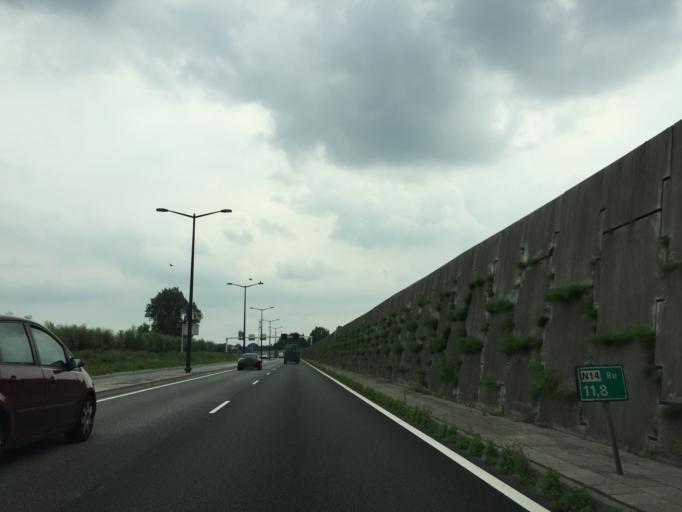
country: NL
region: South Holland
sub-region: Gemeente Leidschendam-Voorburg
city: Voorburg
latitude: 52.0985
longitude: 4.3677
